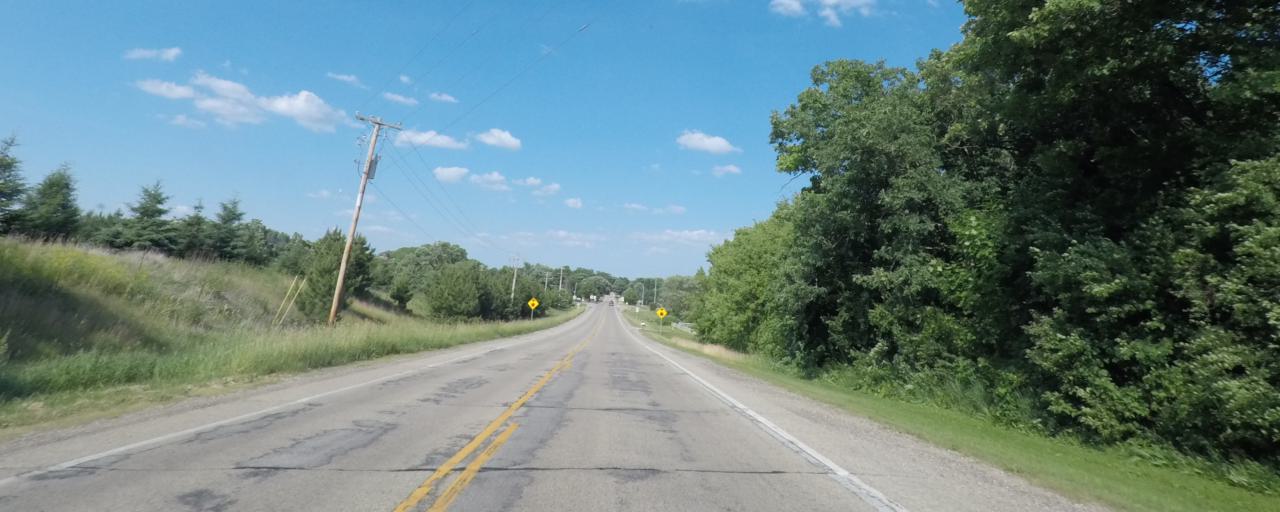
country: US
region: Wisconsin
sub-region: Walworth County
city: Potter Lake
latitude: 42.8288
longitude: -88.3052
